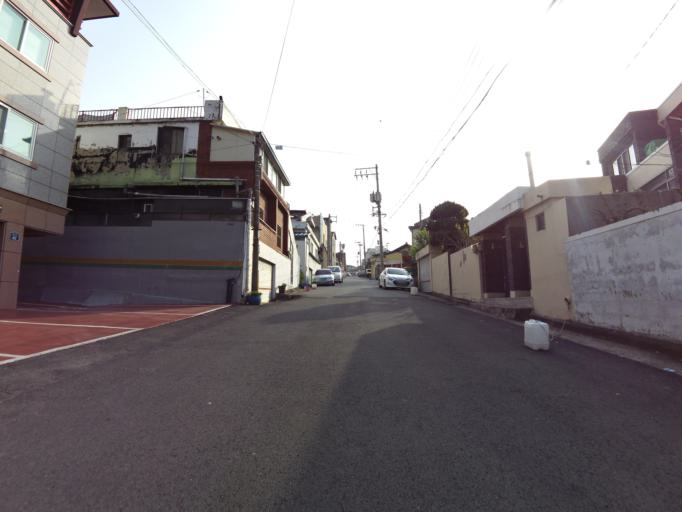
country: KR
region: Daegu
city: Daegu
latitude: 35.8701
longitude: 128.6473
